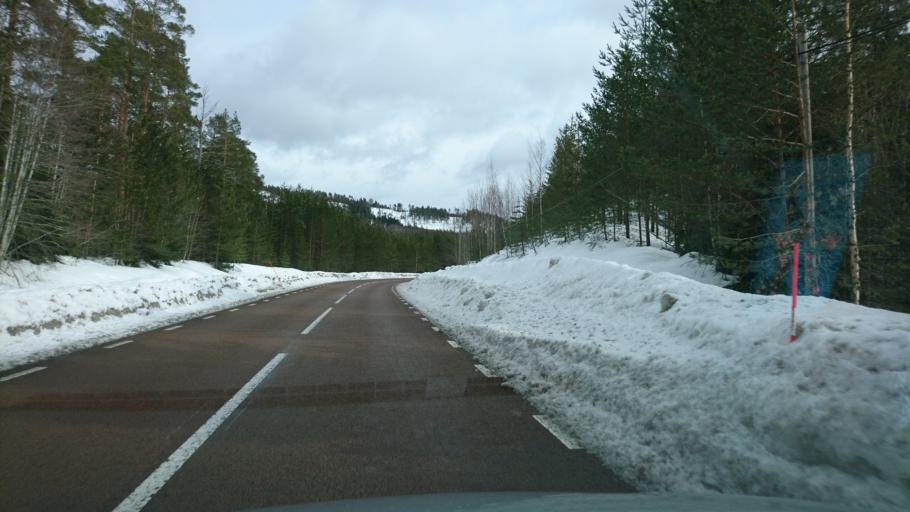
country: SE
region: Vaesternorrland
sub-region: Timra Kommun
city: Bergeforsen
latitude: 62.7878
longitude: 17.4196
